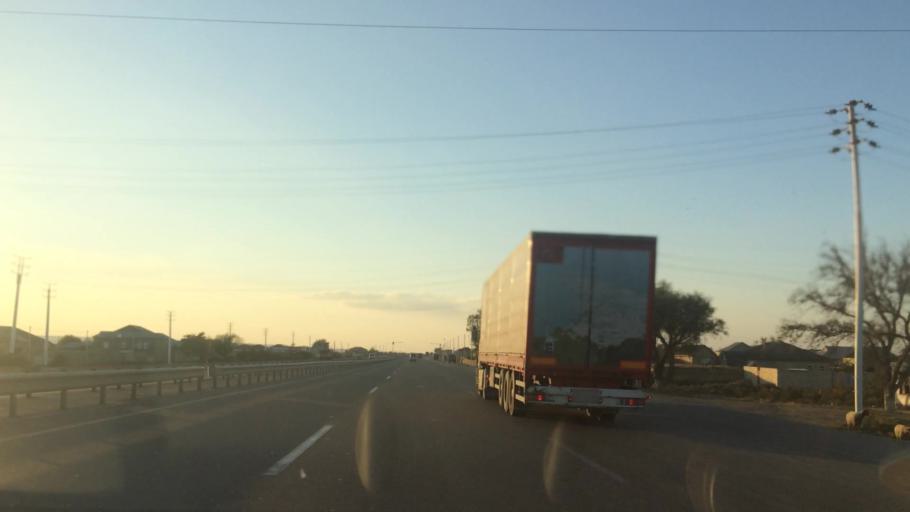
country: AZ
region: Baki
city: Qobustan
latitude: 39.9701
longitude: 49.2663
